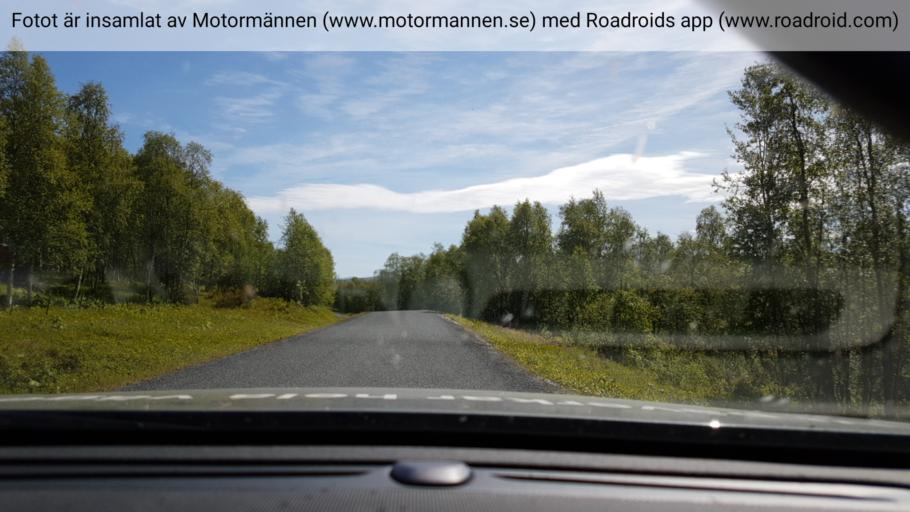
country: NO
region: Nordland
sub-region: Hattfjelldal
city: Hattfjelldal
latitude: 65.3383
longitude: 15.1104
